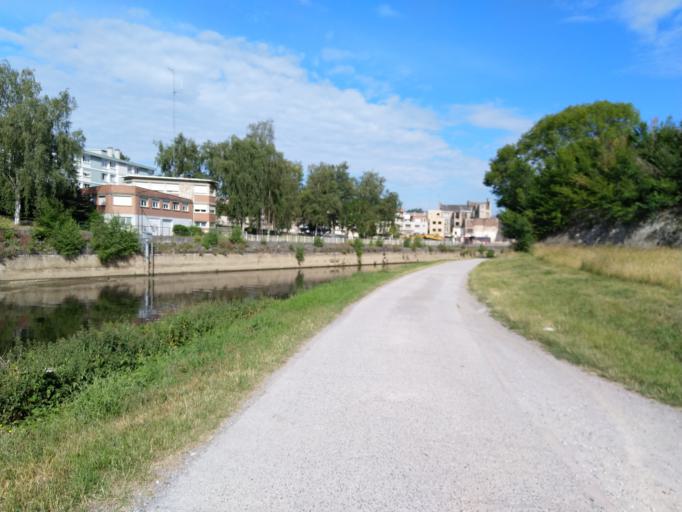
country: FR
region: Nord-Pas-de-Calais
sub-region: Departement du Nord
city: Maubeuge
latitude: 50.2750
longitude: 3.9764
